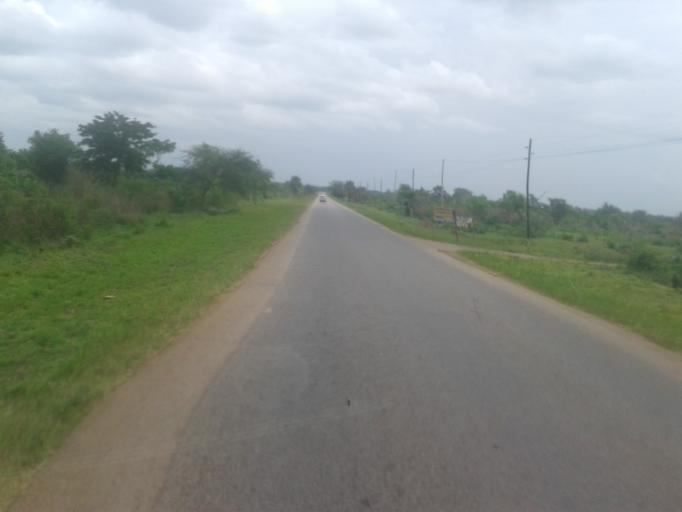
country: UG
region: Western Region
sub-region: Kiryandongo District
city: Masindi Port
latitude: 1.5173
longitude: 32.0615
